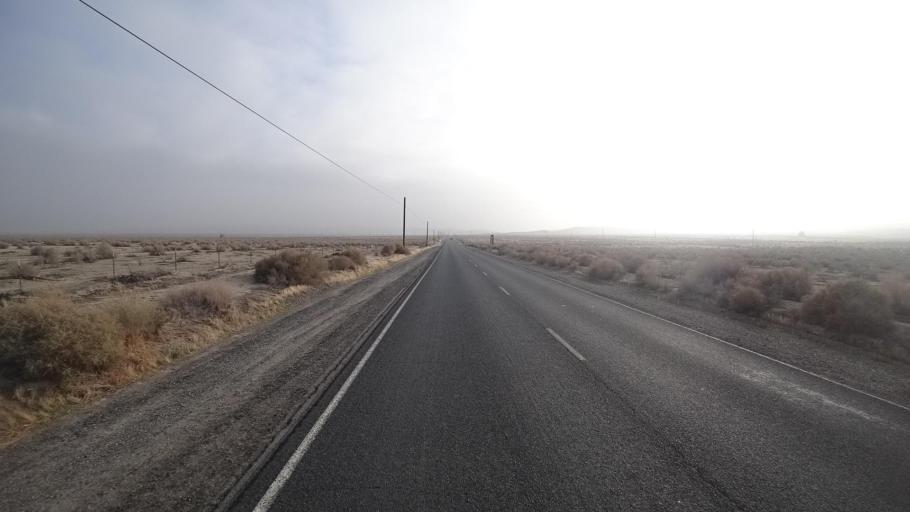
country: US
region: California
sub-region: Kern County
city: Ford City
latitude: 35.2168
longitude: -119.4456
